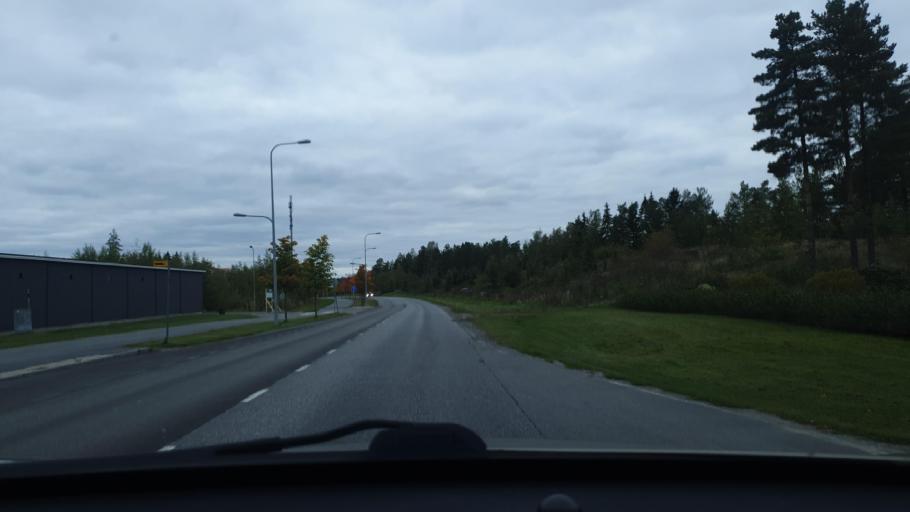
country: FI
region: Ostrobothnia
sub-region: Vaasa
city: Korsholm
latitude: 63.1049
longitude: 21.6750
